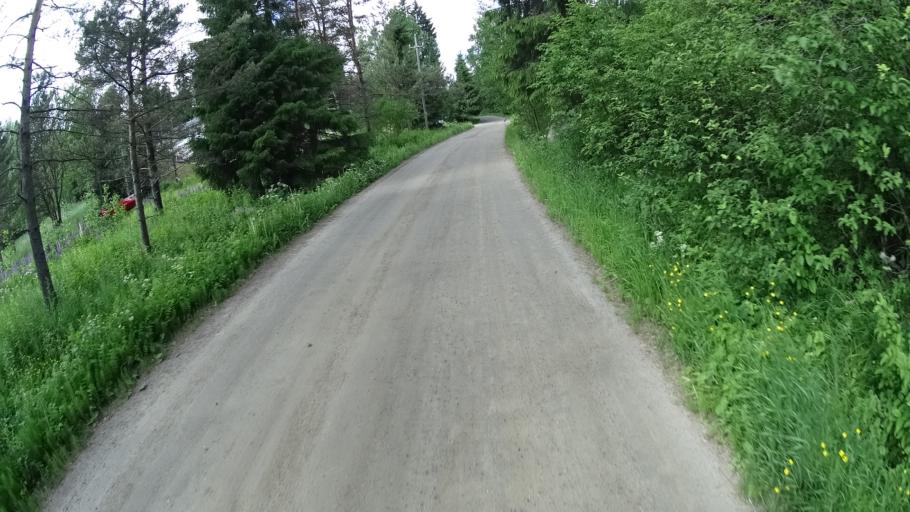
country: FI
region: Uusimaa
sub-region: Helsinki
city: Sibbo
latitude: 60.2755
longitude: 25.3157
